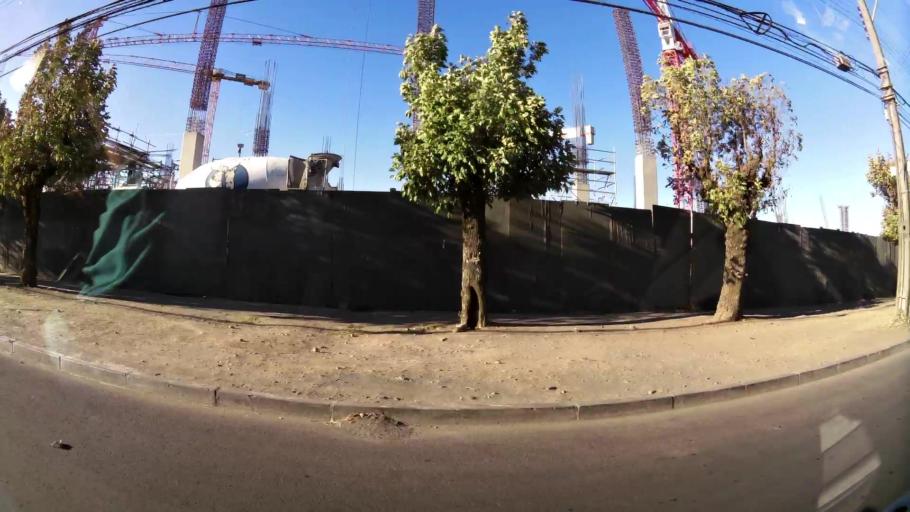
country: CL
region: Maule
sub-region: Provincia de Curico
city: Curico
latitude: -34.9767
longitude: -71.2392
